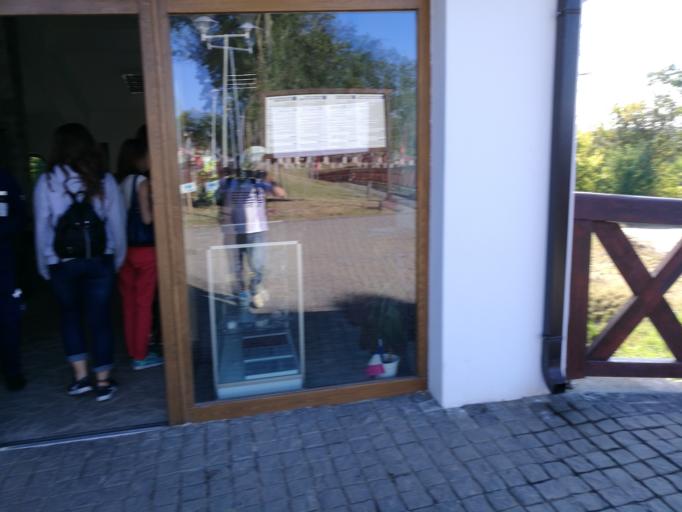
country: RO
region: Suceava
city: Suceava
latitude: 47.6441
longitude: 26.2709
